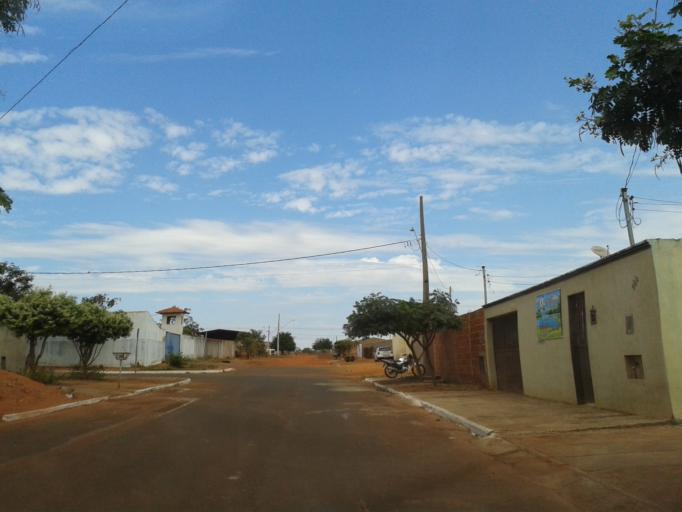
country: BR
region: Minas Gerais
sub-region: Santa Vitoria
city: Santa Vitoria
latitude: -18.8535
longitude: -50.1375
